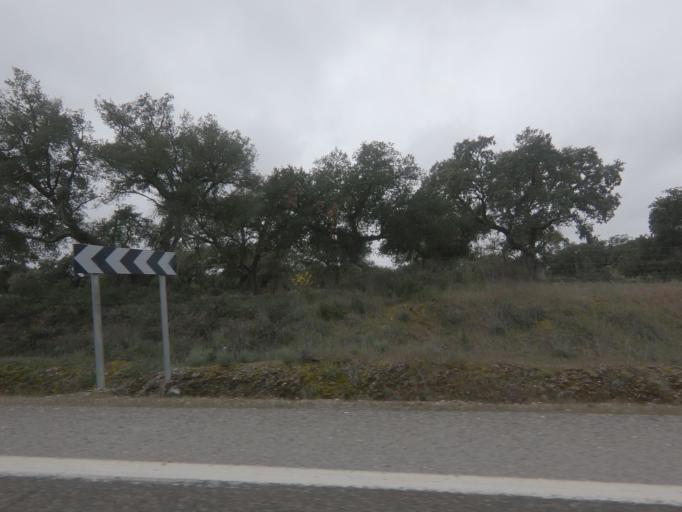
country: ES
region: Extremadura
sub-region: Provincia de Badajoz
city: Puebla de Obando
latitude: 39.2472
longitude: -6.5581
